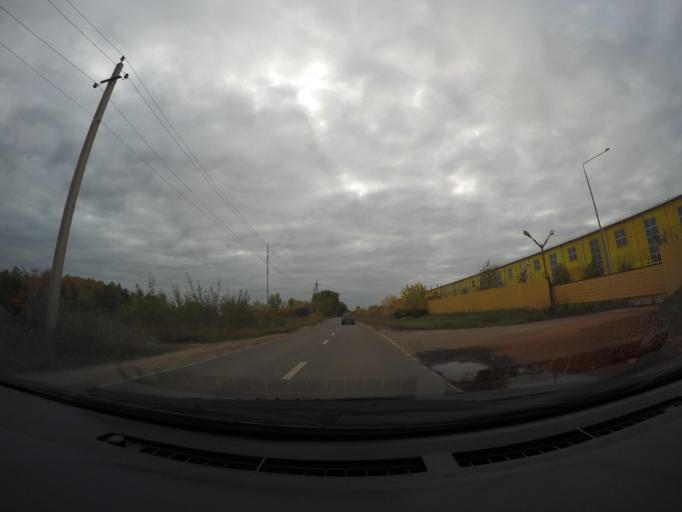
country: RU
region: Moskovskaya
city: Rechitsy
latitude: 55.6161
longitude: 38.4435
